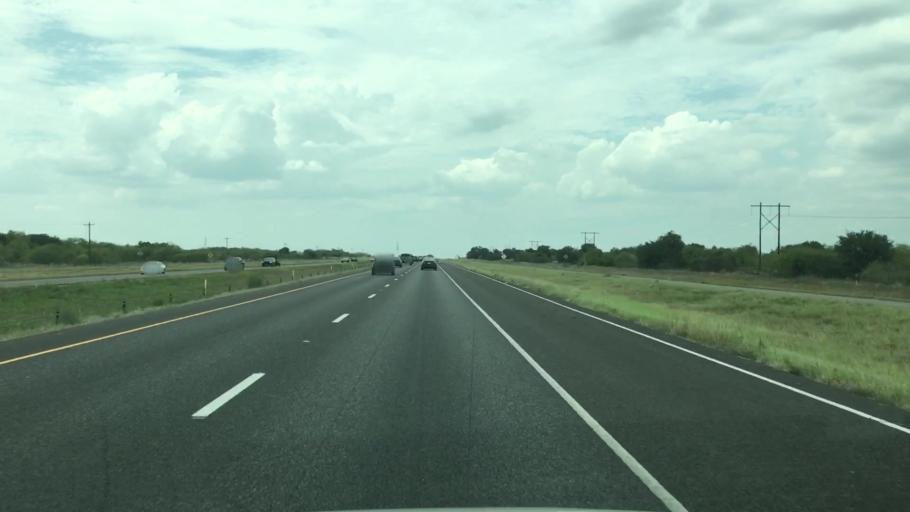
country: US
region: Texas
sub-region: Atascosa County
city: Pleasanton
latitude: 28.8095
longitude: -98.3504
